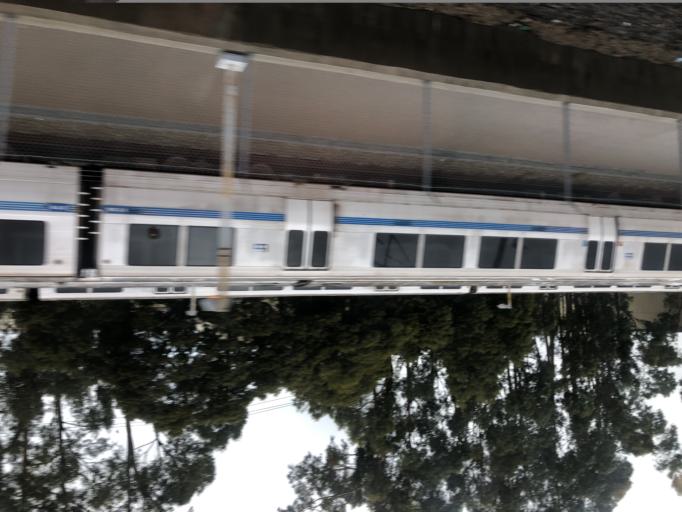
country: US
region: California
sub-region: San Mateo County
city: Millbrae
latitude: 37.5962
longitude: -122.3826
